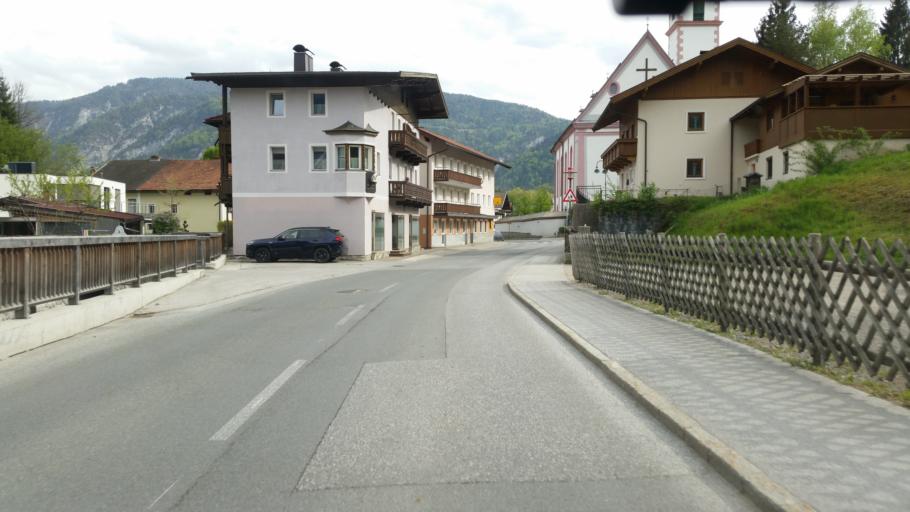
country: AT
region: Tyrol
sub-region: Politischer Bezirk Kufstein
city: Breitenbach am Inn
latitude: 47.4797
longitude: 11.9728
